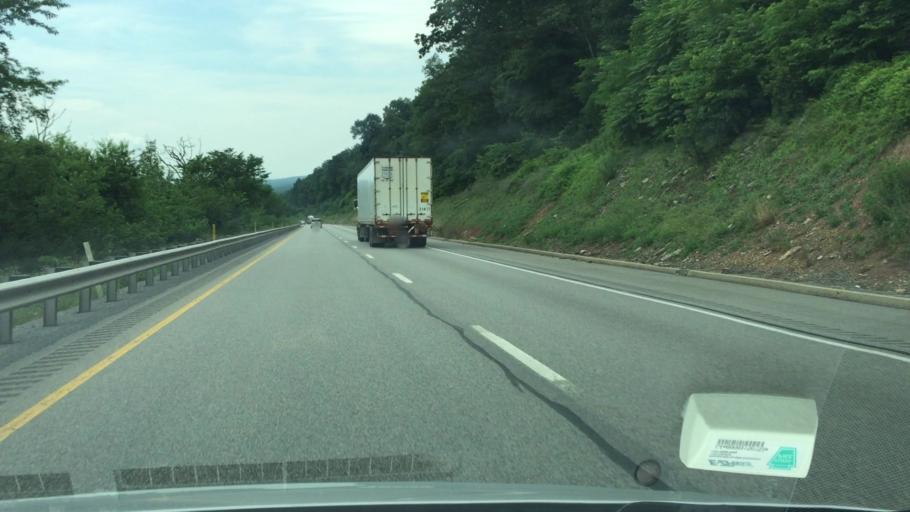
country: US
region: Maryland
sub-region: Washington County
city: Hancock
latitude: 39.8534
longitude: -78.2705
